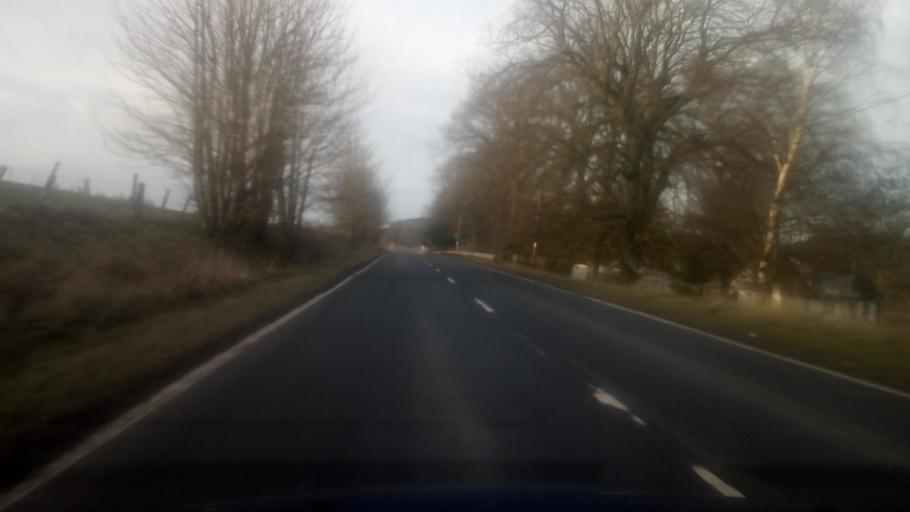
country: GB
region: Scotland
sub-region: The Scottish Borders
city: Jedburgh
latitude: 55.4273
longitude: -2.5308
